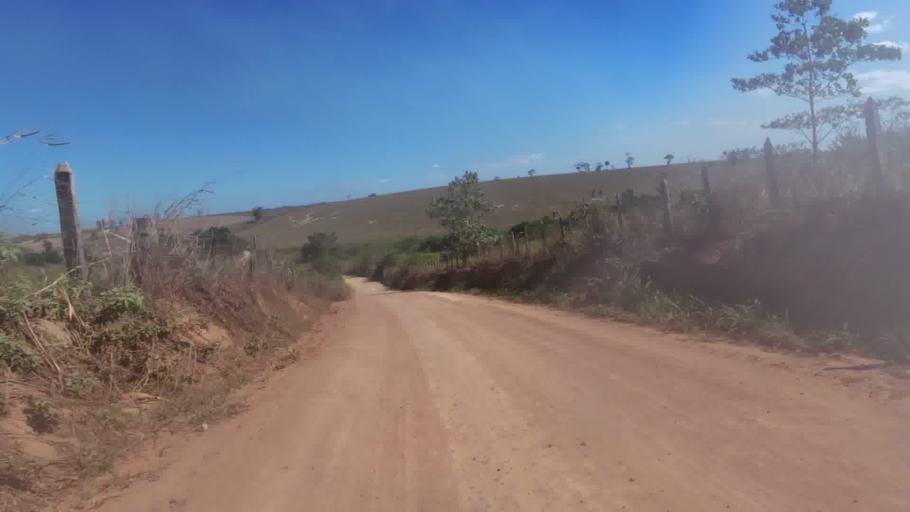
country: BR
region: Espirito Santo
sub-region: Marataizes
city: Marataizes
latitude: -21.1583
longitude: -40.9805
